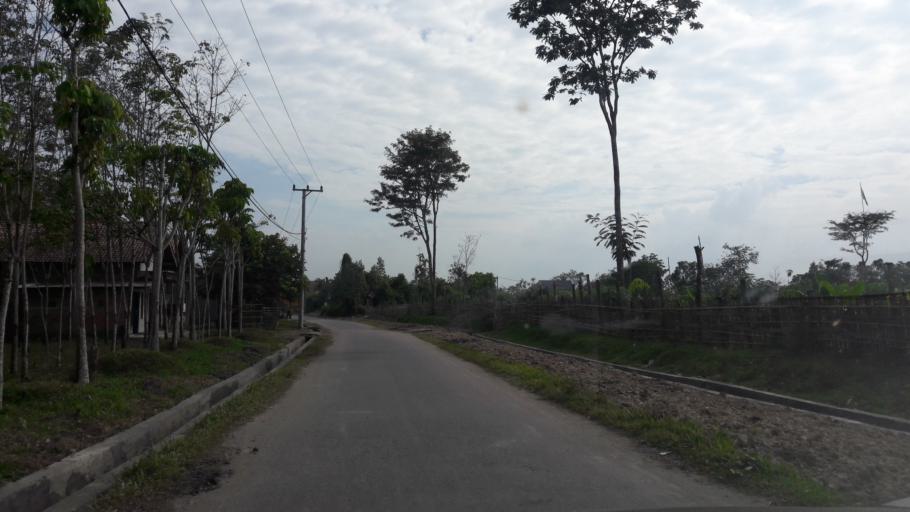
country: ID
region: South Sumatra
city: Gunungmenang
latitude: -3.0944
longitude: 104.0111
